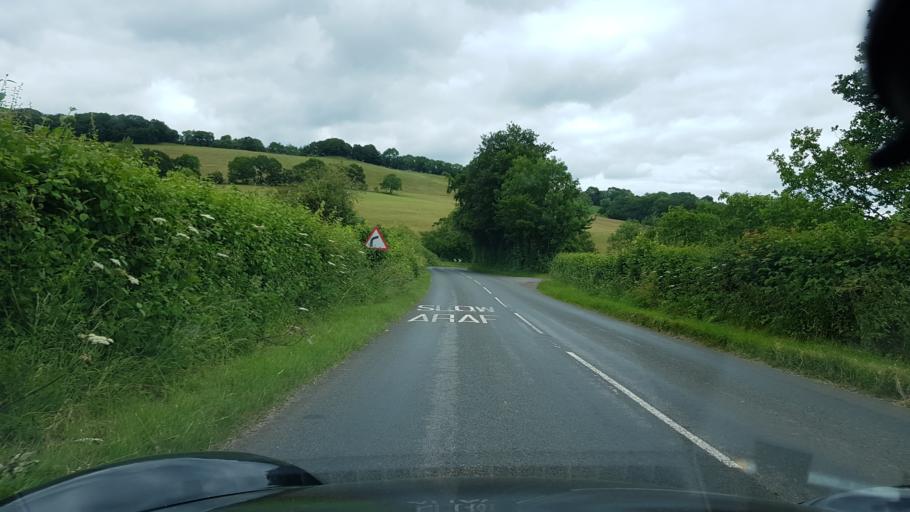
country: GB
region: Wales
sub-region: Monmouthshire
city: Grosmont
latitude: 51.8728
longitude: -2.8589
